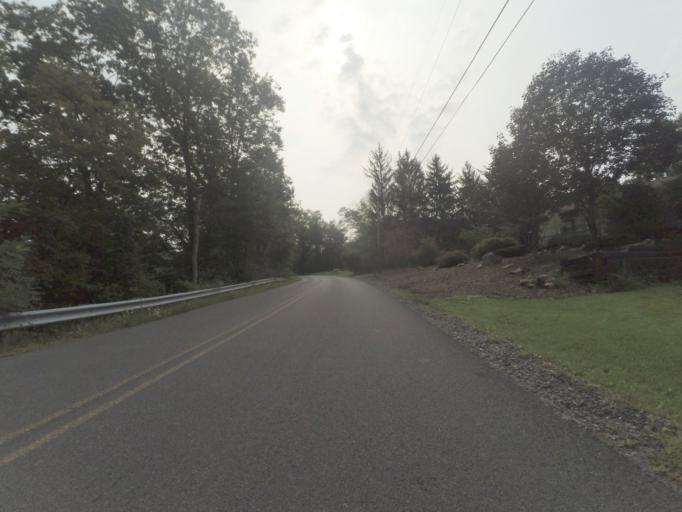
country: US
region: Pennsylvania
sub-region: Huntingdon County
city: McConnellstown
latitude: 40.5363
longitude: -78.0820
